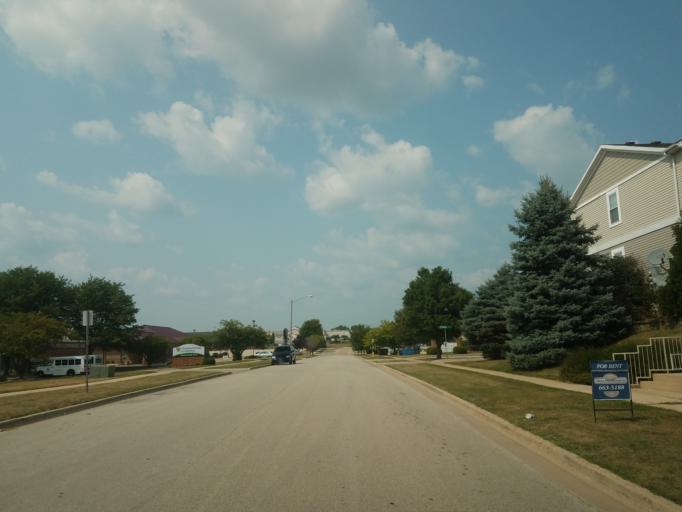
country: US
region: Illinois
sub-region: McLean County
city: Bloomington
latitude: 40.4826
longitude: -88.9463
